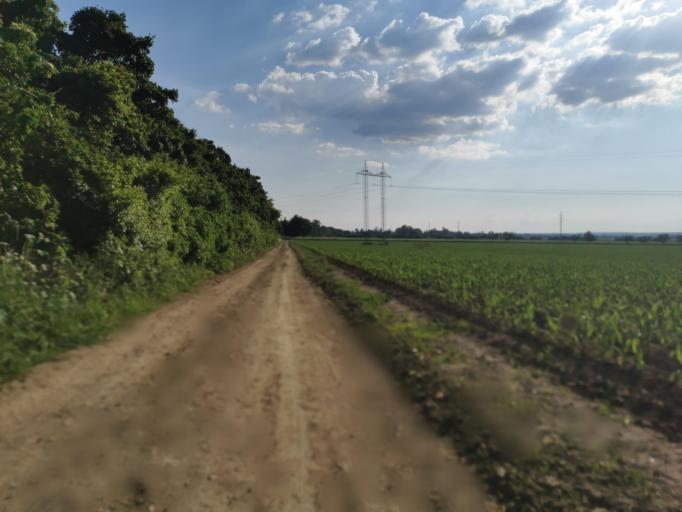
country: CZ
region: South Moravian
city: Straznice
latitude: 48.8846
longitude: 17.3236
